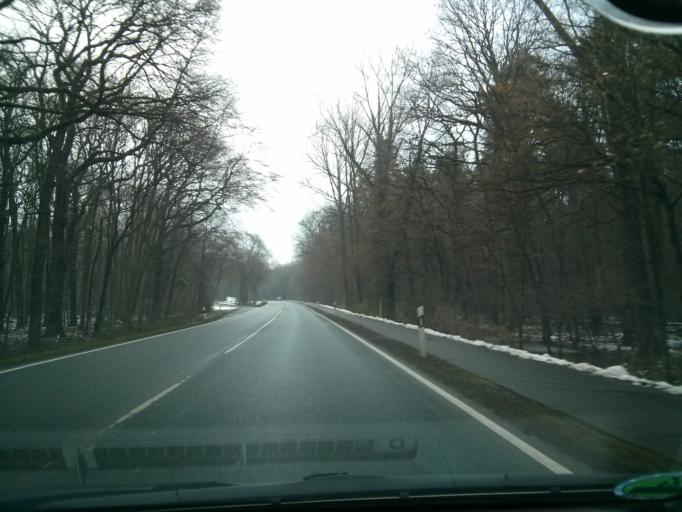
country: DE
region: North Rhine-Westphalia
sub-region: Regierungsbezirk Koln
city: Alfter
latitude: 50.6918
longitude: 7.0008
